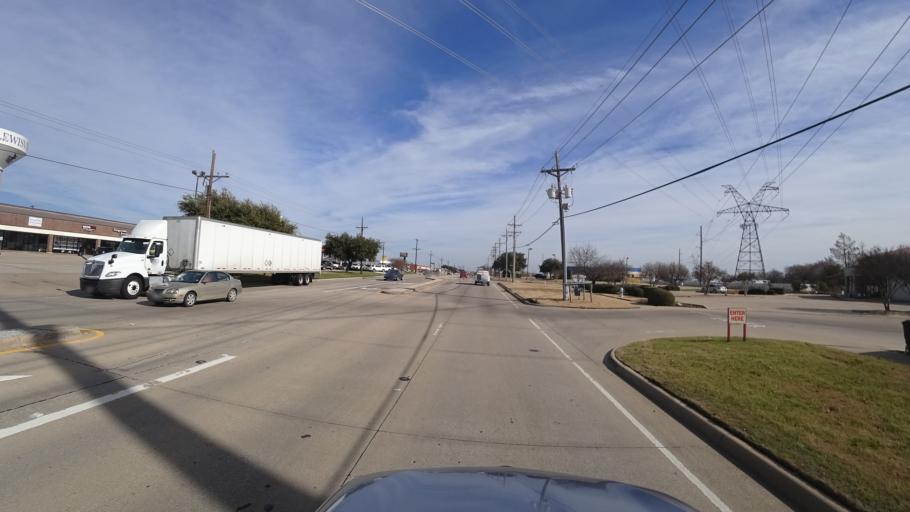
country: US
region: Texas
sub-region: Denton County
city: Highland Village
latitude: 33.0714
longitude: -97.0330
